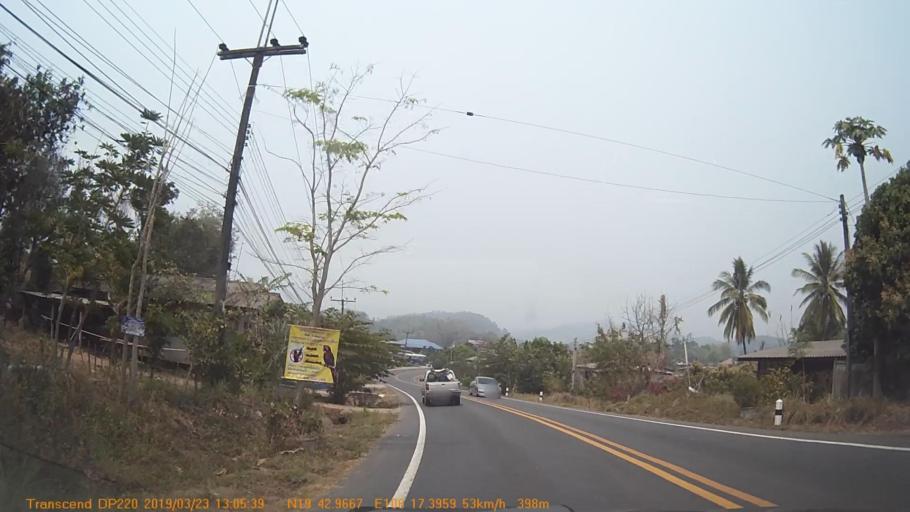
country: TH
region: Chiang Rai
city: Thoeng
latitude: 19.7163
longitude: 100.2900
